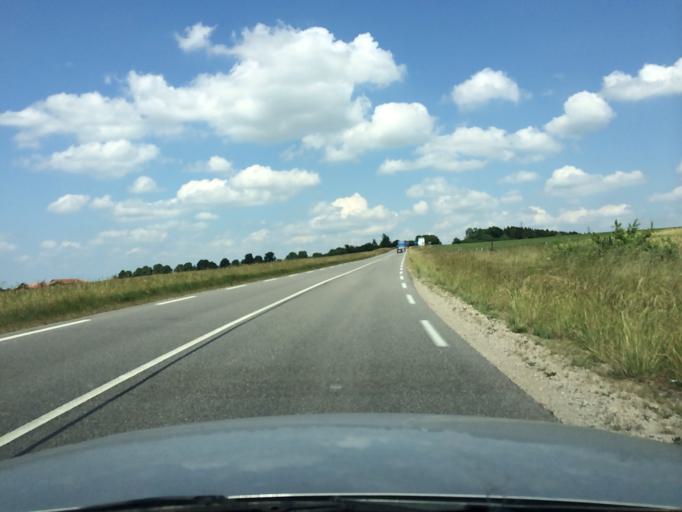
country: FR
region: Lorraine
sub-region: Departement de la Moselle
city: Lorquin
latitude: 48.6376
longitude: 6.8998
